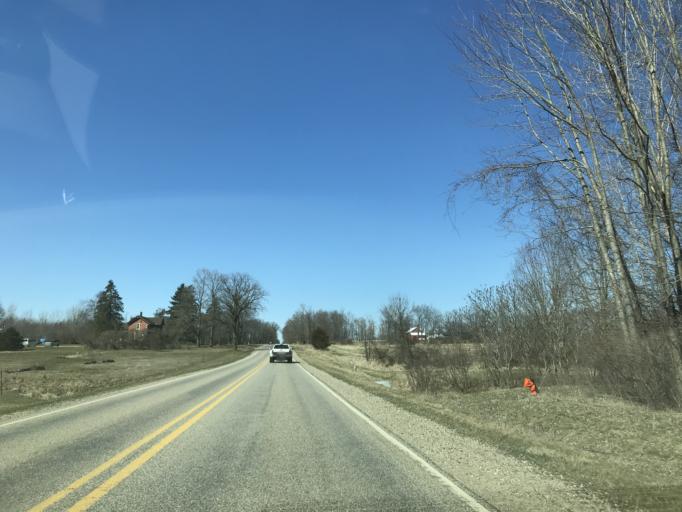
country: US
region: Michigan
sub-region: Hillsdale County
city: Litchfield
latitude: 41.9857
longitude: -84.8084
